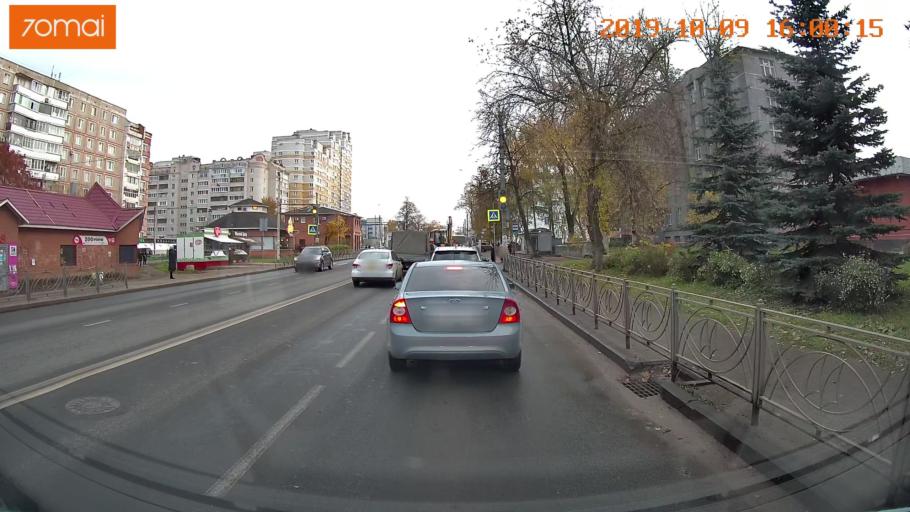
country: RU
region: Kostroma
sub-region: Kostromskoy Rayon
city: Kostroma
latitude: 57.7661
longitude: 40.9511
